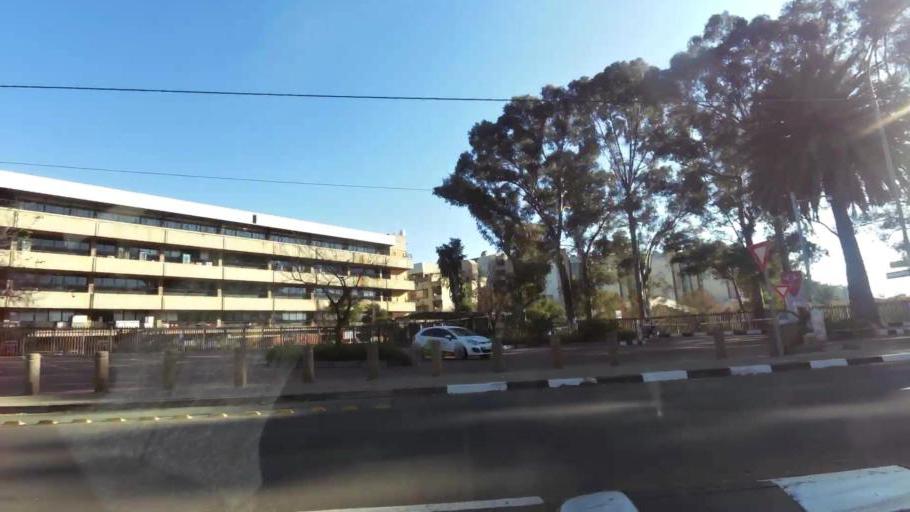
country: ZA
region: Gauteng
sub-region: City of Johannesburg Metropolitan Municipality
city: Johannesburg
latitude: -26.1859
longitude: 27.9984
